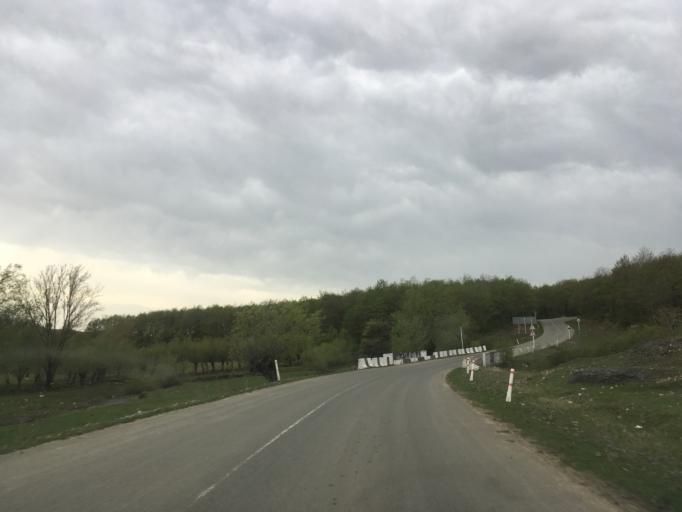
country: GE
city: Surami
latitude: 42.2026
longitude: 43.4008
